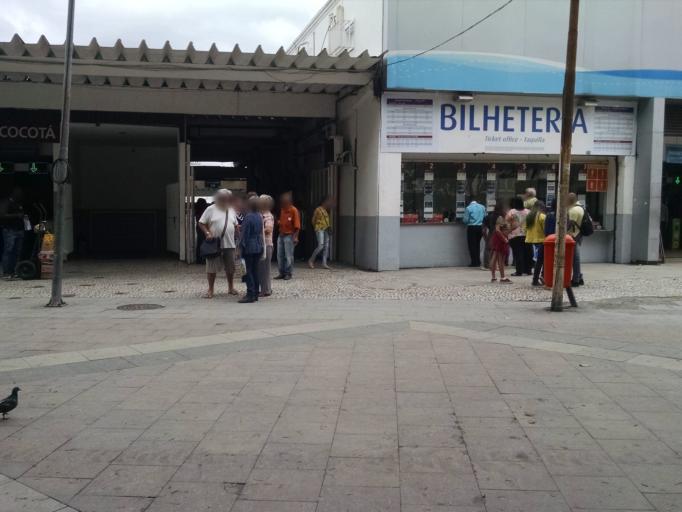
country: BR
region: Rio de Janeiro
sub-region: Rio De Janeiro
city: Rio de Janeiro
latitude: -22.9027
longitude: -43.1725
